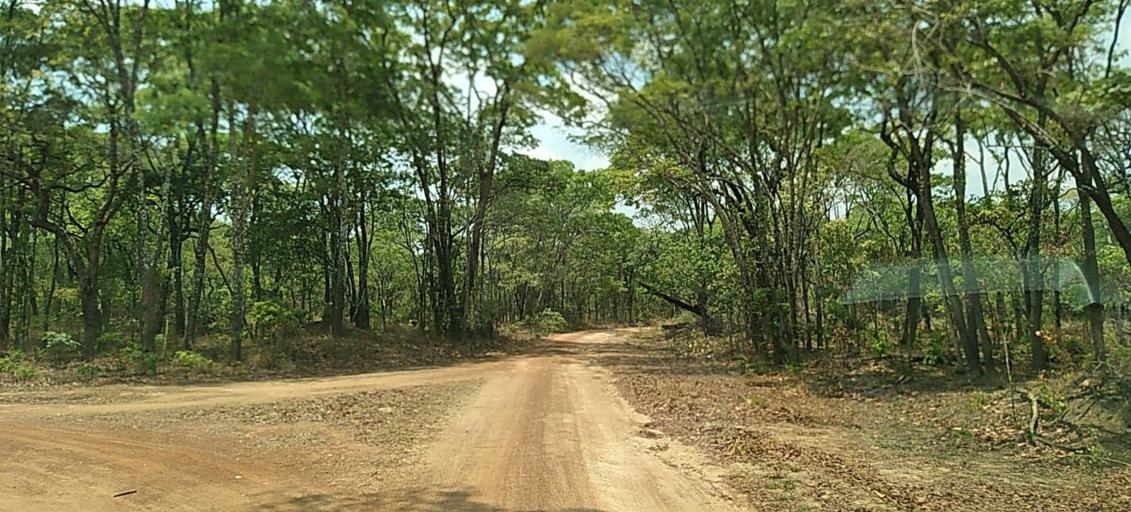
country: ZM
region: Copperbelt
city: Chingola
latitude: -12.7722
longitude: 27.6795
